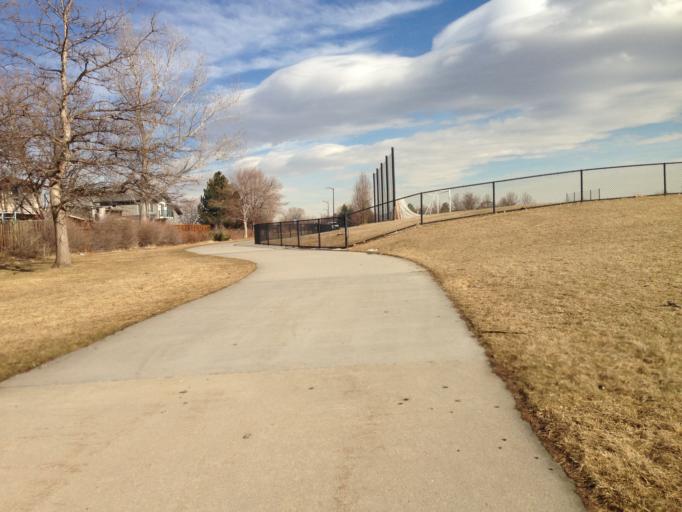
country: US
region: Colorado
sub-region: Boulder County
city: Boulder
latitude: 39.9930
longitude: -105.2259
